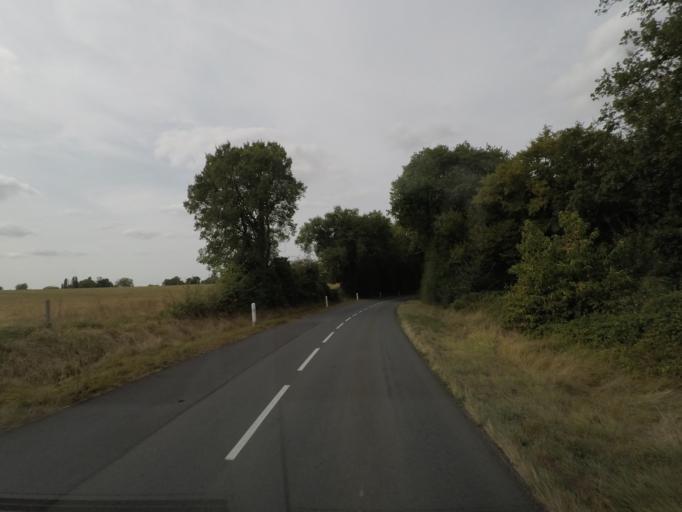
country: FR
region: Poitou-Charentes
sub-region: Departement de la Charente
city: Nanteuil-en-Vallee
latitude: 45.9925
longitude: 0.3323
